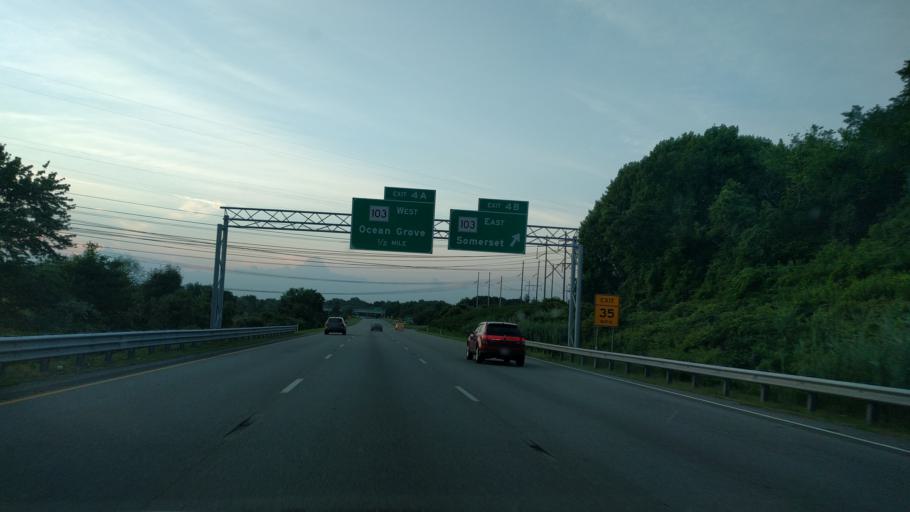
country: US
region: Massachusetts
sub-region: Bristol County
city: Ocean Grove
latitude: 41.7204
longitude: -71.1833
